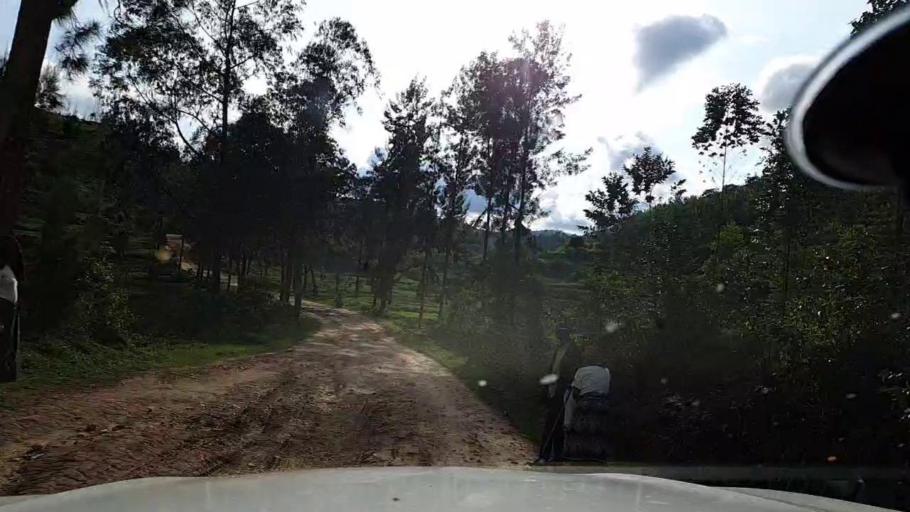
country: RW
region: Southern Province
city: Gitarama
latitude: -2.1671
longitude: 29.5580
